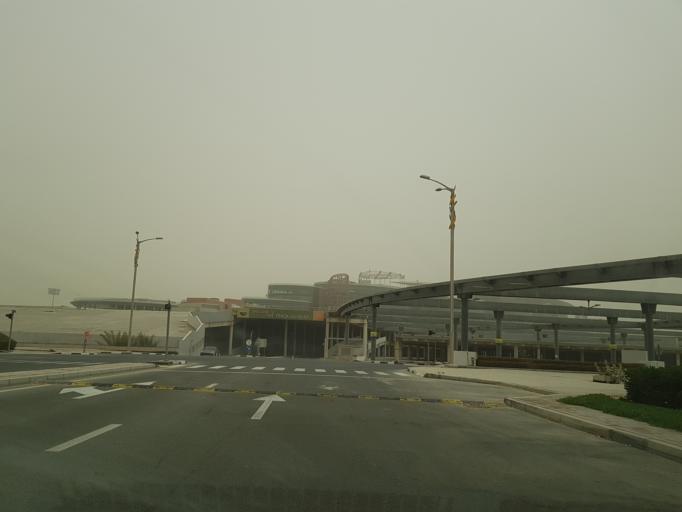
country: AE
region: Dubai
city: Dubai
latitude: 25.1629
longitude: 55.3033
